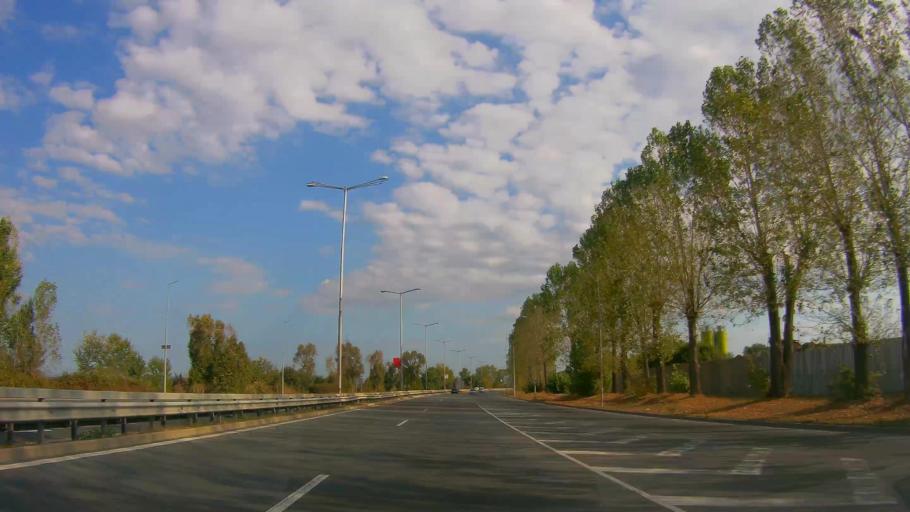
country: BG
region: Burgas
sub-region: Obshtina Burgas
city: Burgas
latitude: 42.4772
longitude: 27.4358
